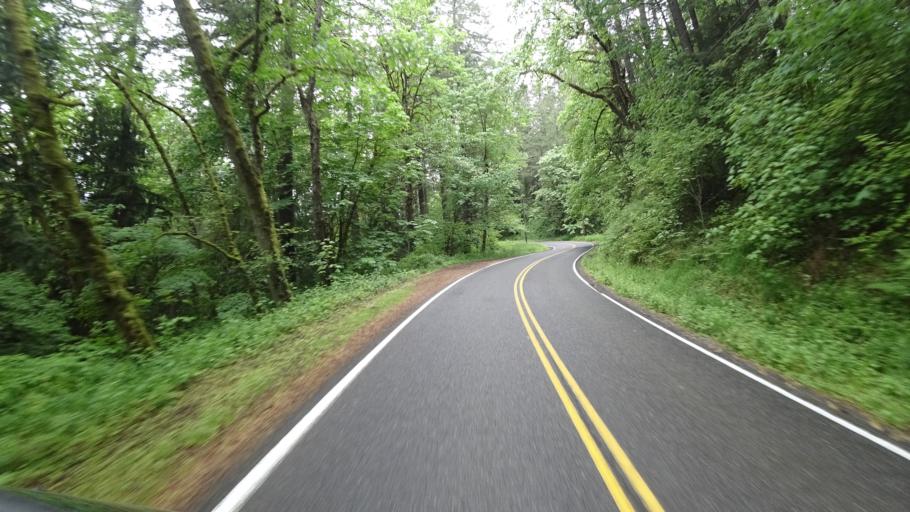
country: US
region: Oregon
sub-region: Washington County
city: West Haven-Sylvan
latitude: 45.5408
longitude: -122.7441
